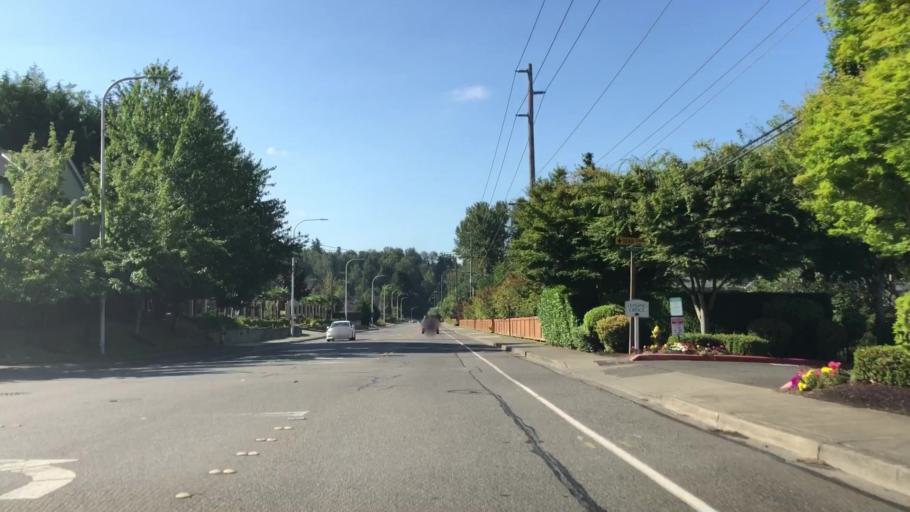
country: US
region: Washington
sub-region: King County
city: East Hill-Meridian
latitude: 47.4336
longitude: -122.2131
